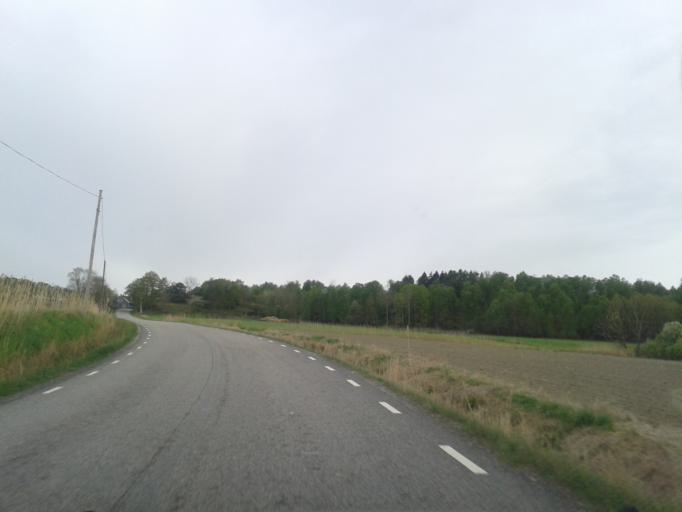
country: SE
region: Vaestra Goetaland
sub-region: Stenungsunds Kommun
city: Stora Hoga
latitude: 57.9754
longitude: 11.8287
